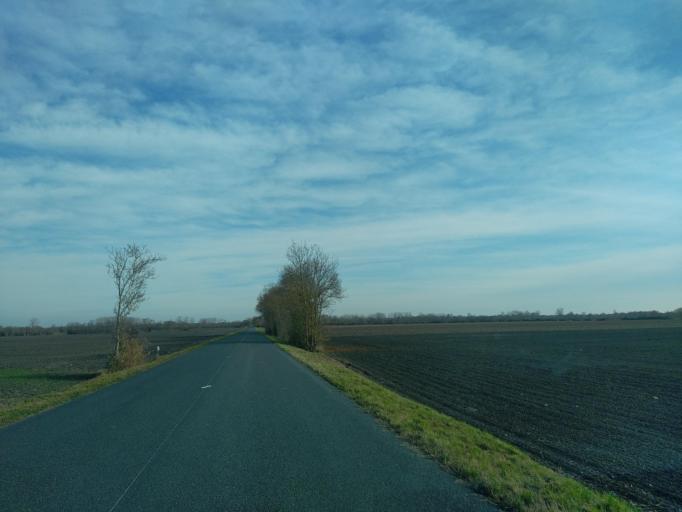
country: FR
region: Pays de la Loire
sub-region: Departement de la Vendee
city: Maillezais
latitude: 46.3789
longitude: -0.7765
